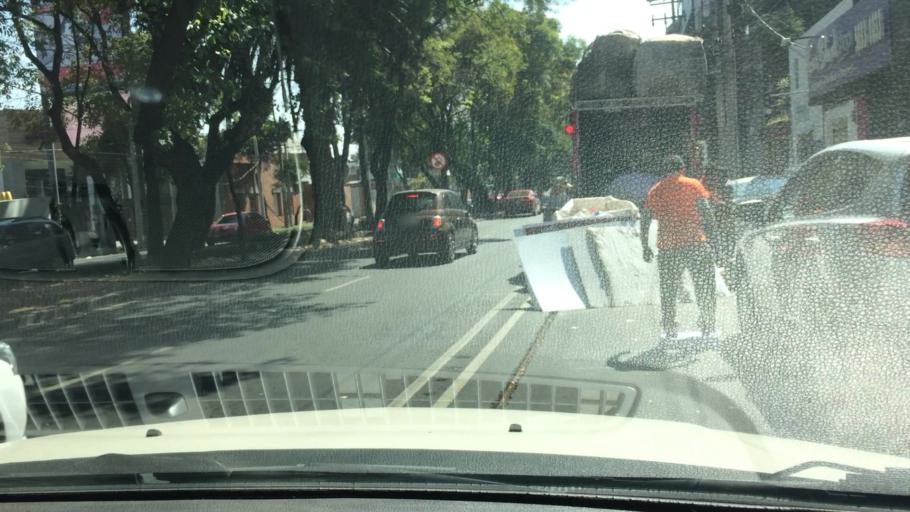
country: MX
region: Mexico City
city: Coyoacan
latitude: 19.3509
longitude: -99.1513
